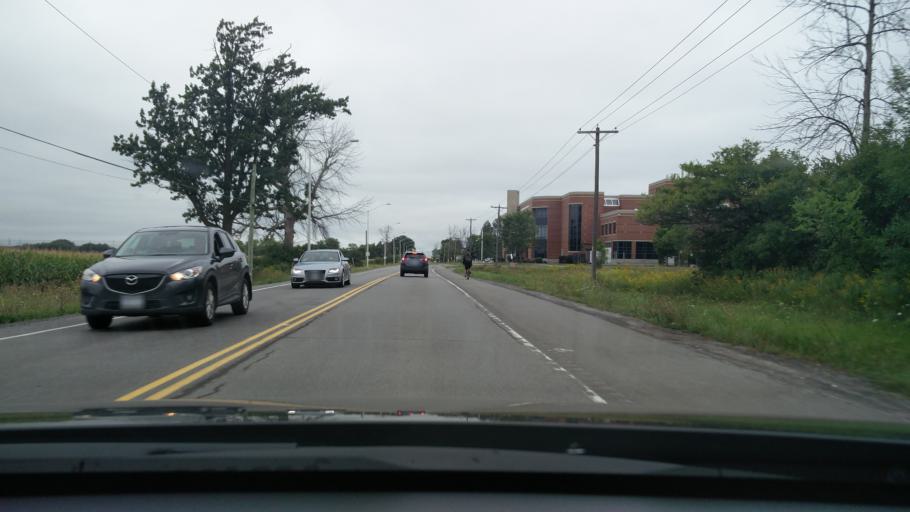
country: CA
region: Ontario
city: Bells Corners
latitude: 45.2607
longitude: -75.7405
